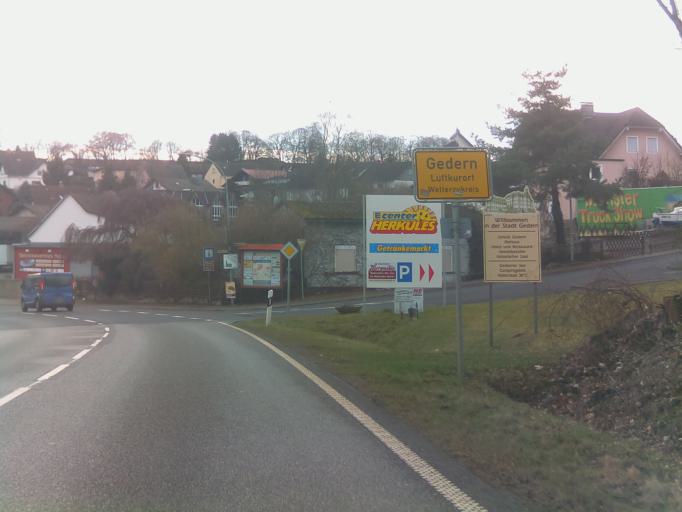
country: DE
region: Hesse
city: Gedern
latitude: 50.4306
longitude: 9.1976
